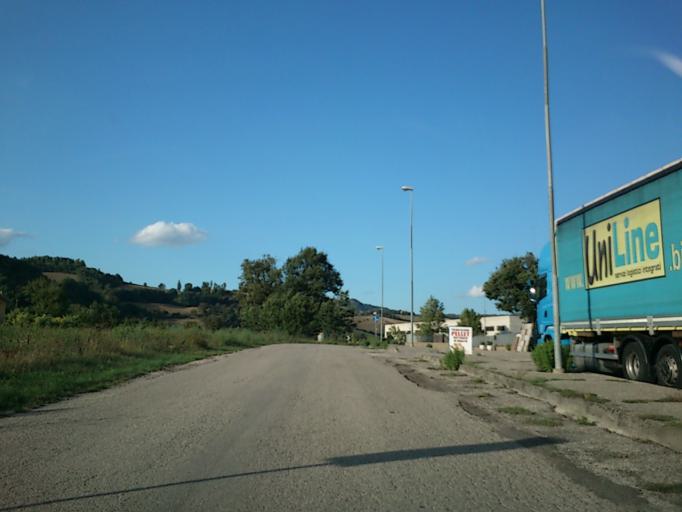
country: IT
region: The Marches
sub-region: Provincia di Pesaro e Urbino
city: Fermignano
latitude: 43.6888
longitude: 12.6456
